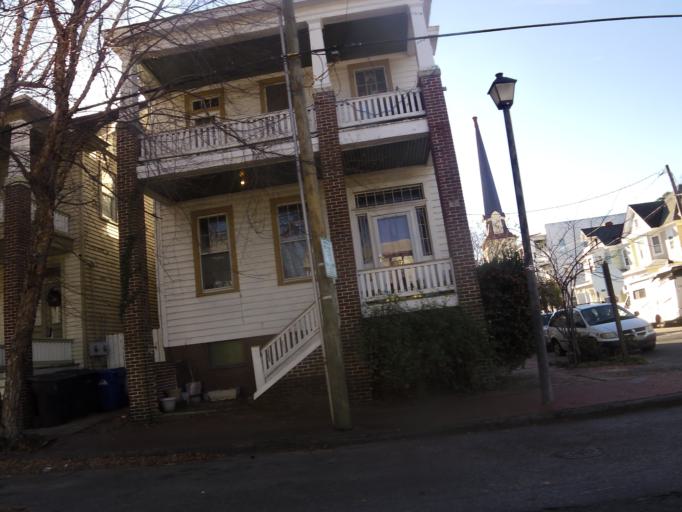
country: US
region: Virginia
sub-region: City of Portsmouth
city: Portsmouth
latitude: 36.8368
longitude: -76.3023
